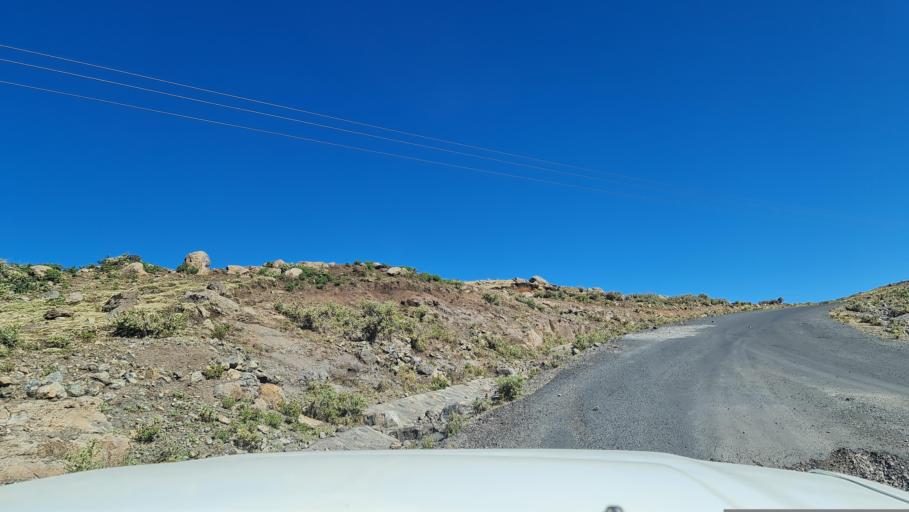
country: ET
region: Amhara
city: Debark'
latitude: 13.1399
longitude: 38.1769
